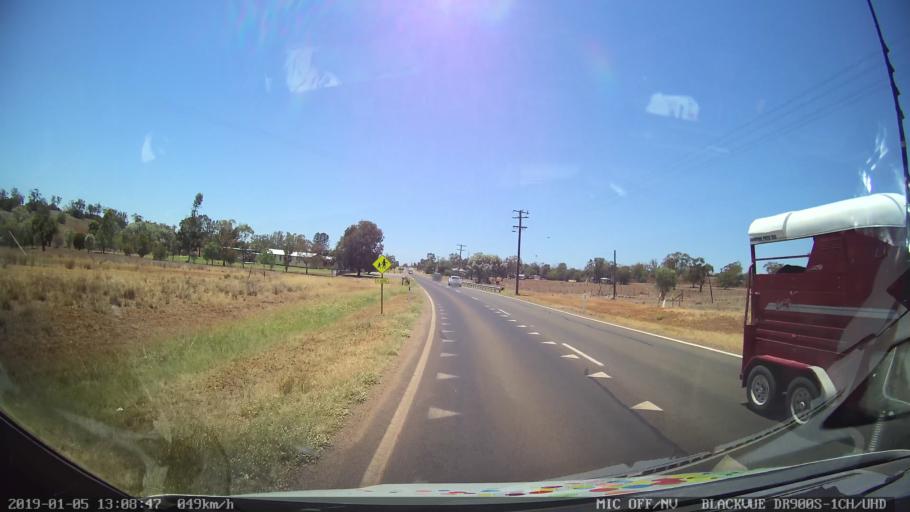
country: AU
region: New South Wales
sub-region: Gunnedah
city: Gunnedah
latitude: -31.0999
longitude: 149.9052
